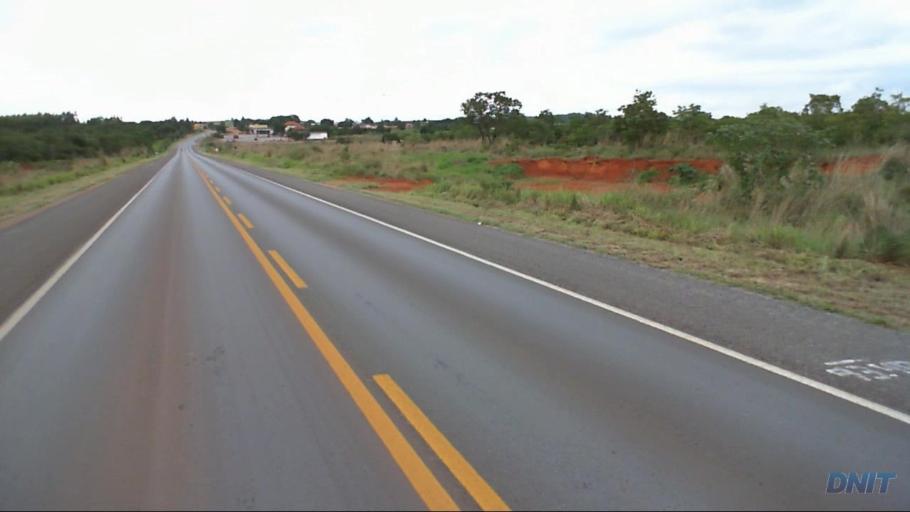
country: BR
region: Goias
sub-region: Barro Alto
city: Barro Alto
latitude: -15.2091
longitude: -48.6917
